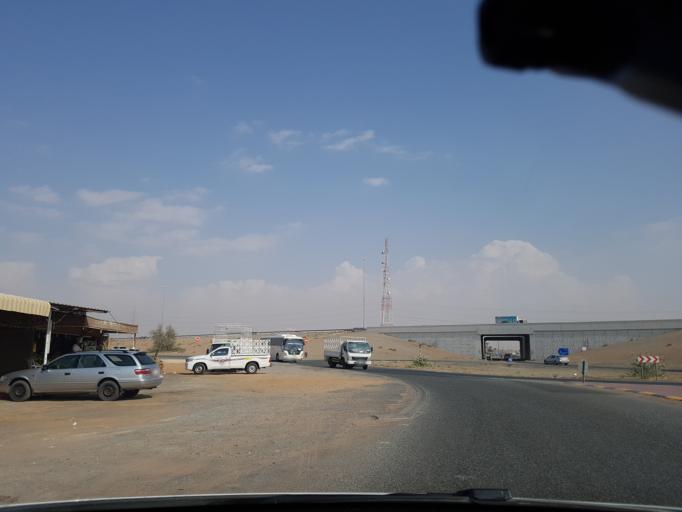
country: AE
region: Umm al Qaywayn
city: Umm al Qaywayn
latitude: 25.5286
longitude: 55.7225
